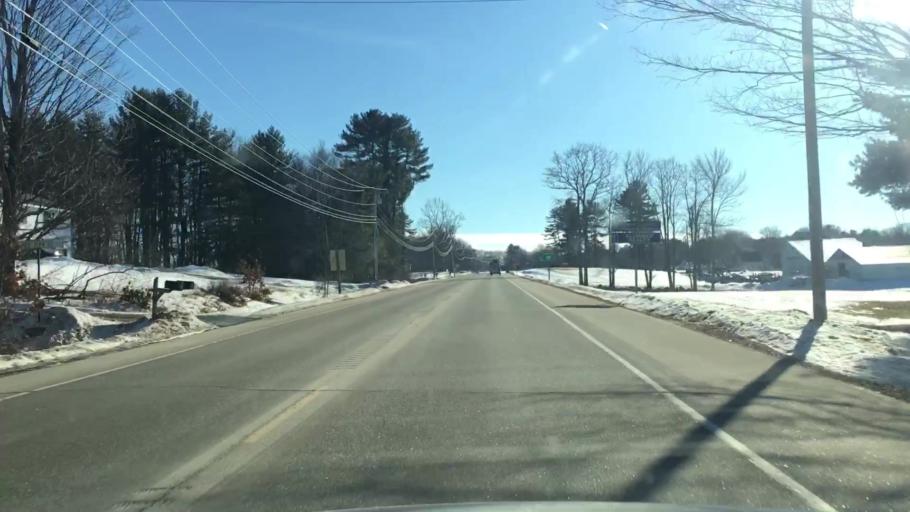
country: US
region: Maine
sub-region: Cumberland County
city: North Windham
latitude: 43.8071
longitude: -70.4040
